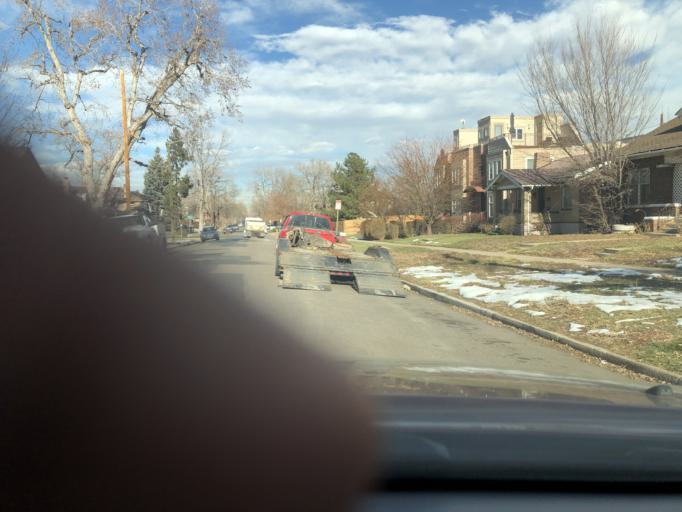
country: US
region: Colorado
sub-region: Denver County
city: Denver
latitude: 39.7548
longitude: -104.9622
